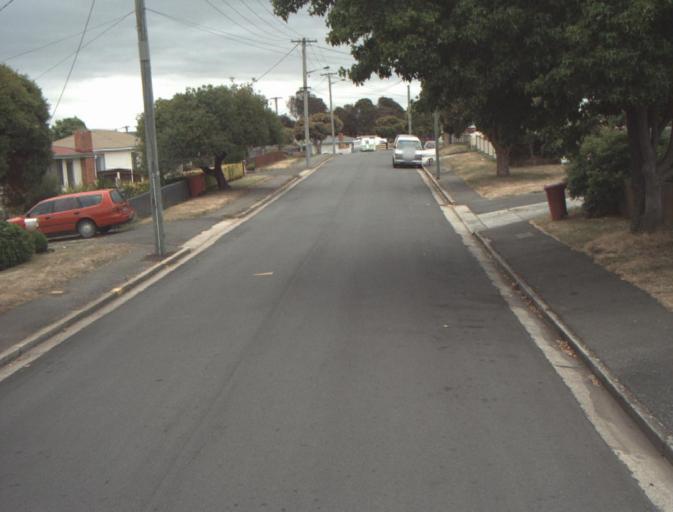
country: AU
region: Tasmania
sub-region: Launceston
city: Newstead
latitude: -41.4319
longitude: 147.1854
